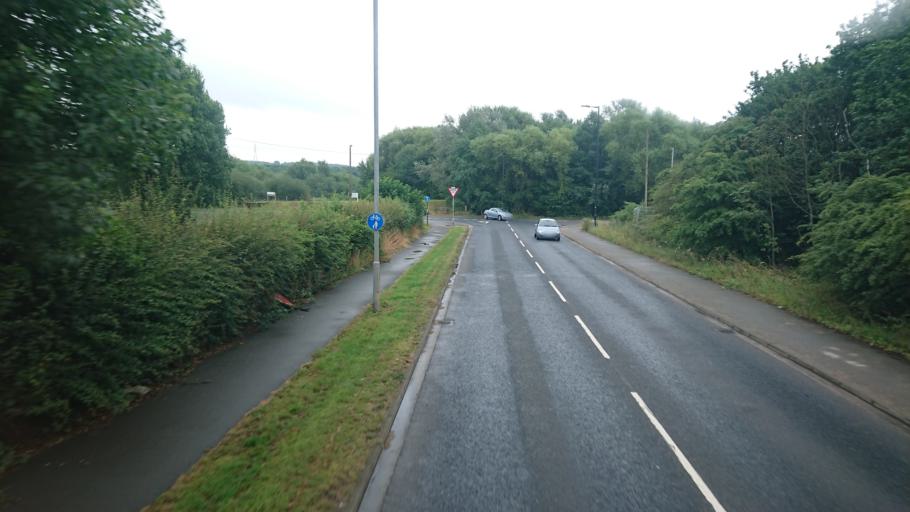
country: GB
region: England
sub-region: Rotherham
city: Orgreave
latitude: 53.3882
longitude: -1.3662
